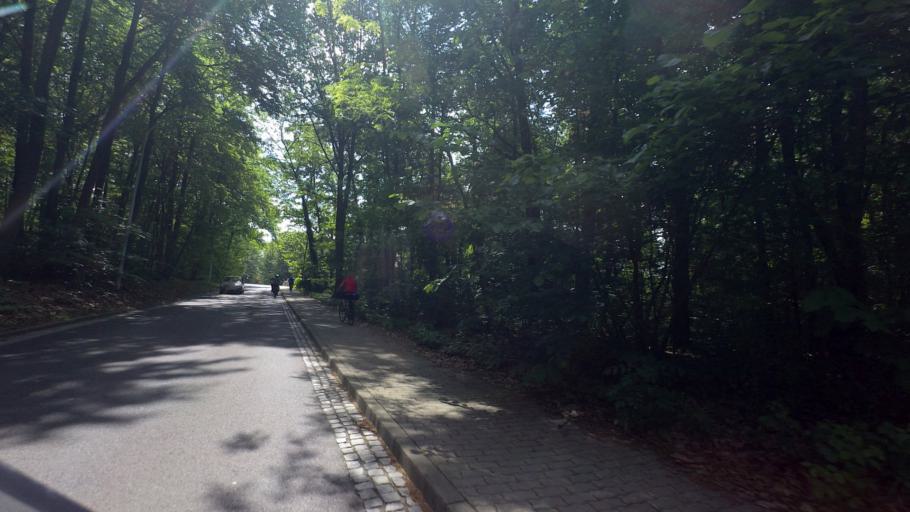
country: DE
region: Saxony
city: Weisswasser
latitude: 51.5009
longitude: 14.6150
